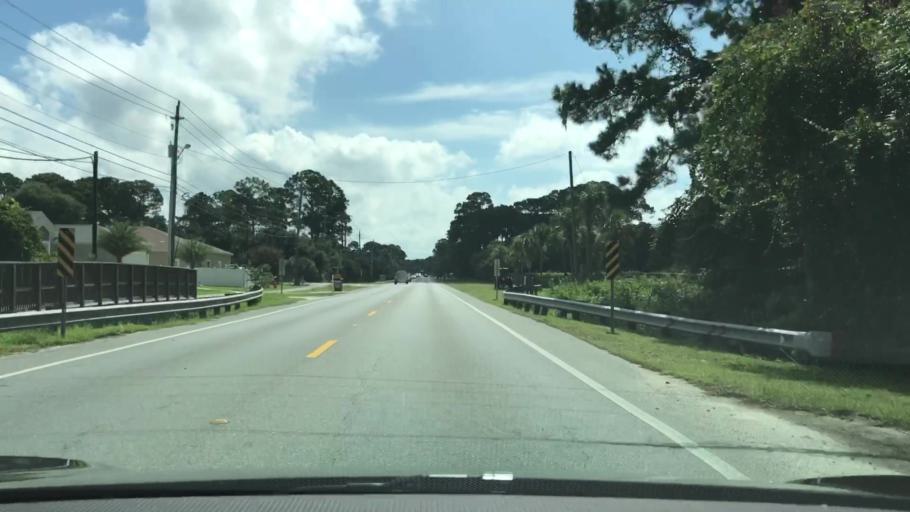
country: US
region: Florida
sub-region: Bay County
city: Panama City Beach
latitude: 30.1667
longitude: -85.7784
